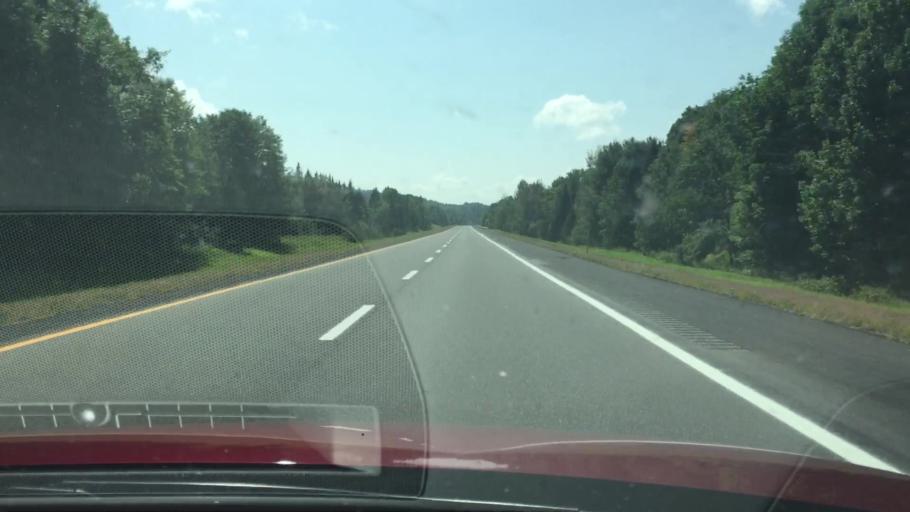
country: US
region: Maine
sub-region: Penobscot County
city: Patten
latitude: 45.9282
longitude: -68.3639
